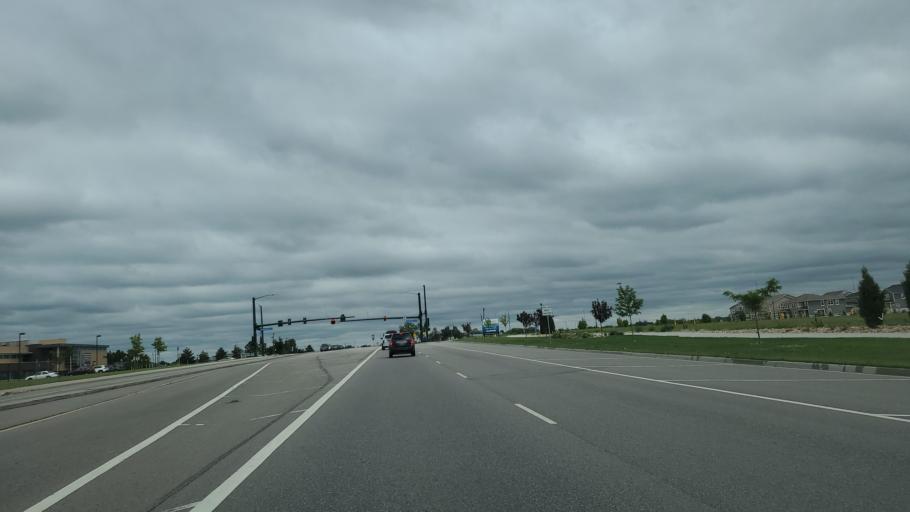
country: US
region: Colorado
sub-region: Adams County
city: Brighton
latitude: 39.9143
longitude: -104.8359
